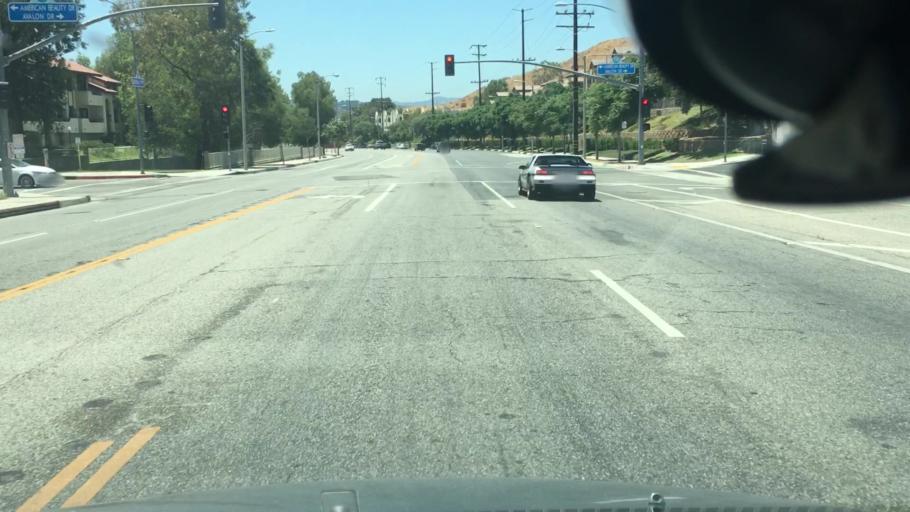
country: US
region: California
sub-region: Los Angeles County
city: Santa Clarita
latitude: 34.4228
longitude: -118.4518
